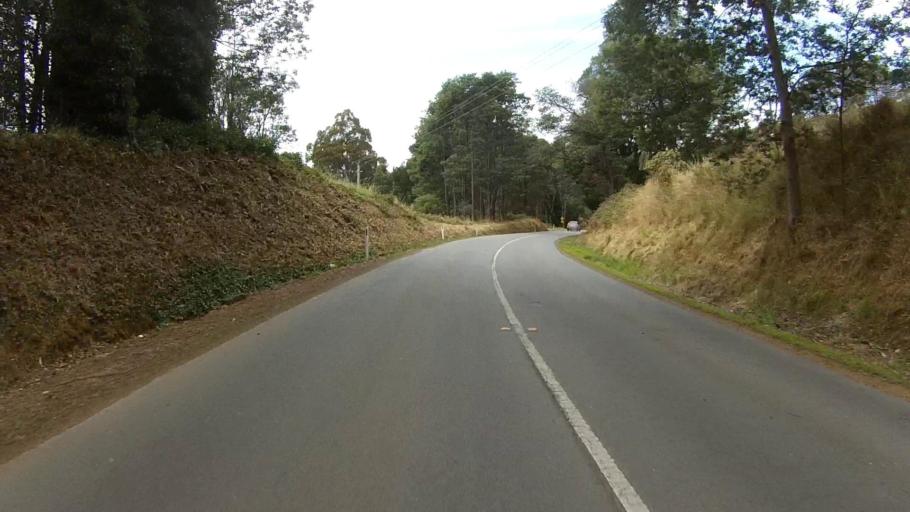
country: AU
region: Tasmania
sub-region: Kingborough
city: Kettering
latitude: -43.1106
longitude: 147.1979
